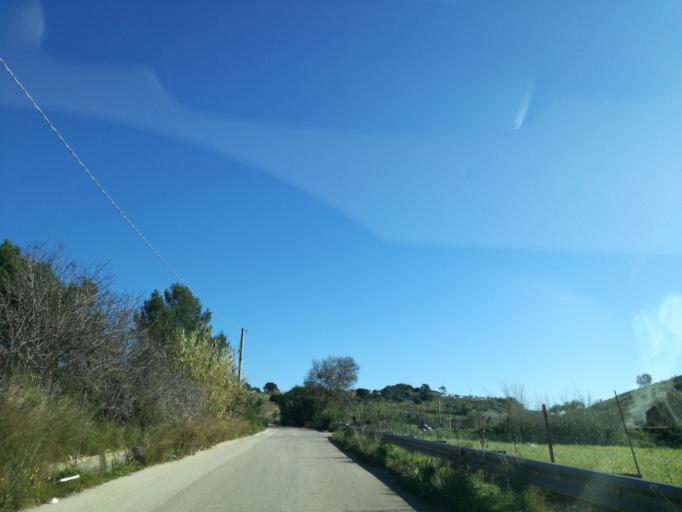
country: IT
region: Sicily
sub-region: Provincia di Caltanissetta
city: Niscemi
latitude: 37.0611
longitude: 14.3446
